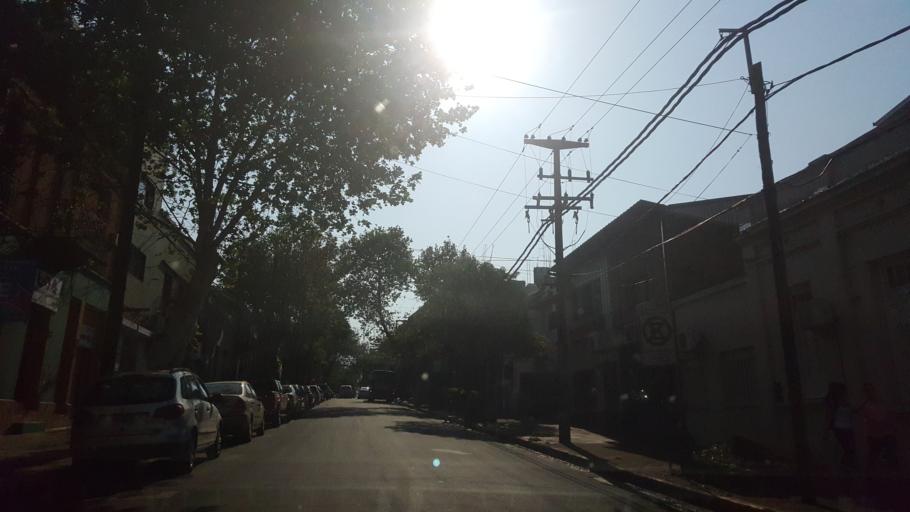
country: AR
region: Misiones
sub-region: Departamento de Capital
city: Posadas
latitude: -27.3654
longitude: -55.8912
